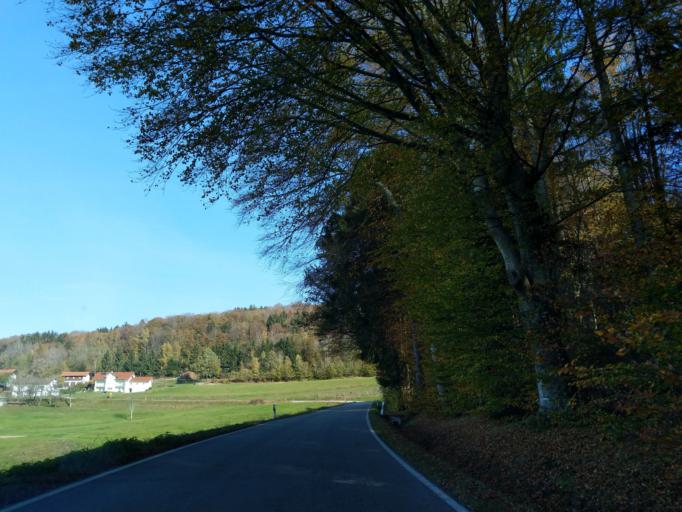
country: DE
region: Bavaria
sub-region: Lower Bavaria
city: Grattersdorf
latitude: 48.7974
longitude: 13.1877
